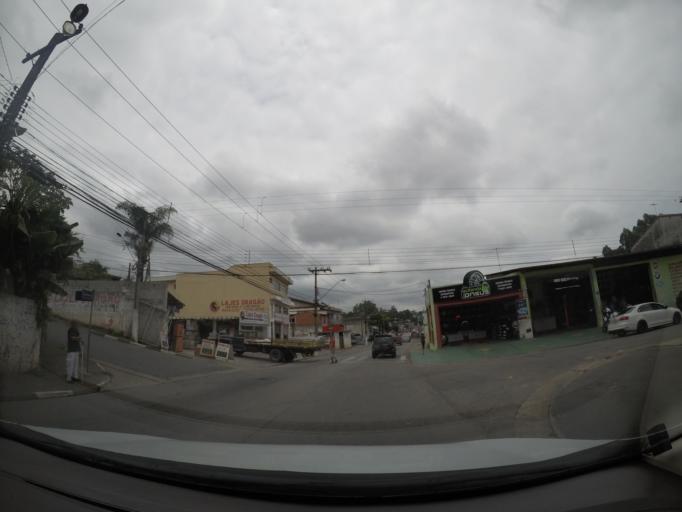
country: BR
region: Sao Paulo
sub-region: Aruja
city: Aruja
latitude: -23.3935
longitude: -46.3199
